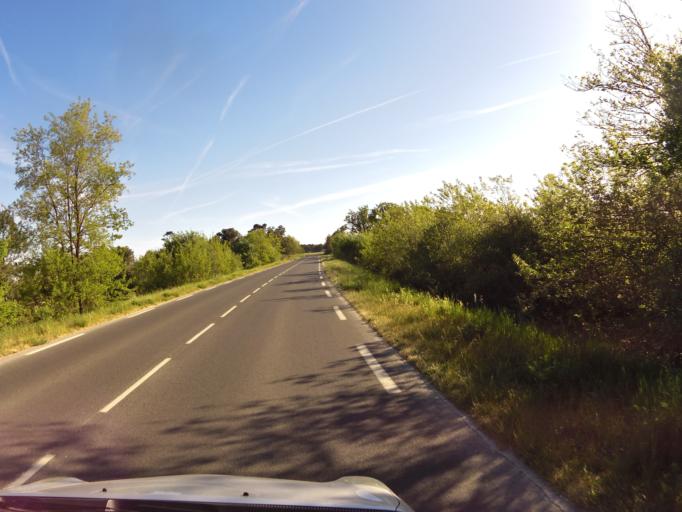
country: FR
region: Aquitaine
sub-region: Departement de la Dordogne
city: Sarlat-la-Caneda
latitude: 44.9532
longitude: 1.2245
